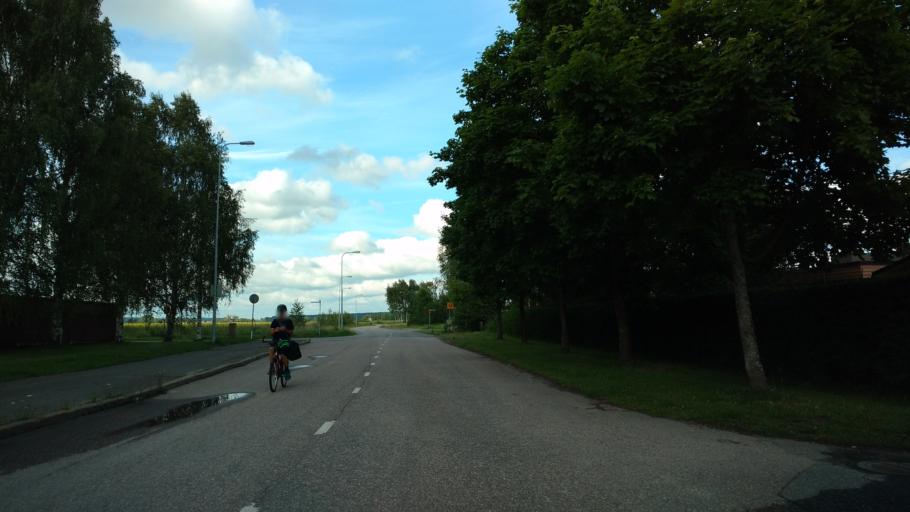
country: FI
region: Varsinais-Suomi
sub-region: Salo
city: Salo
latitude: 60.3997
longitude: 23.1502
